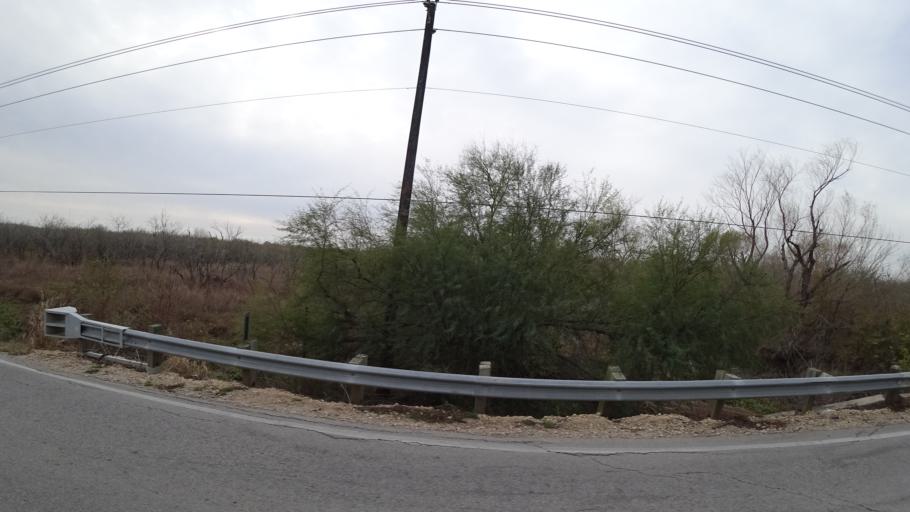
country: US
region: Texas
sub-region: Travis County
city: Garfield
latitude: 30.1513
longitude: -97.6342
